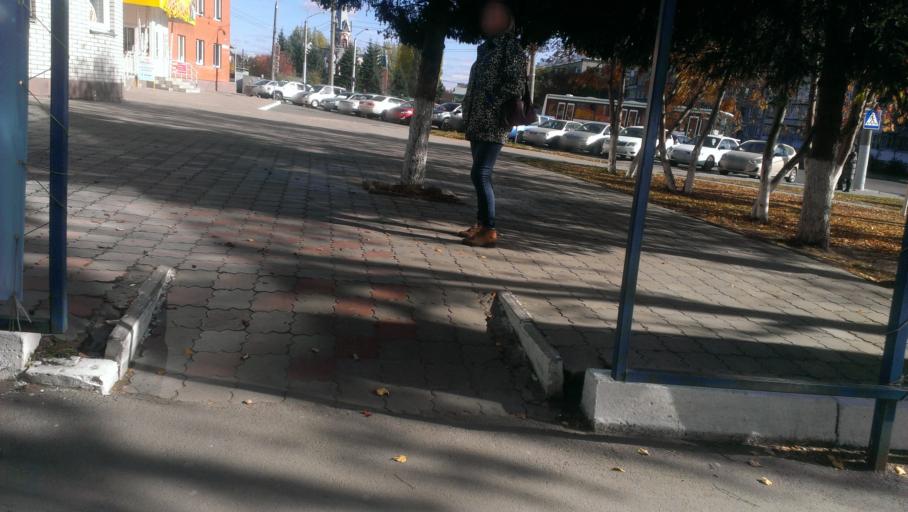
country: RU
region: Altai Krai
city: Novosilikatnyy
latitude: 53.3551
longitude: 83.6843
